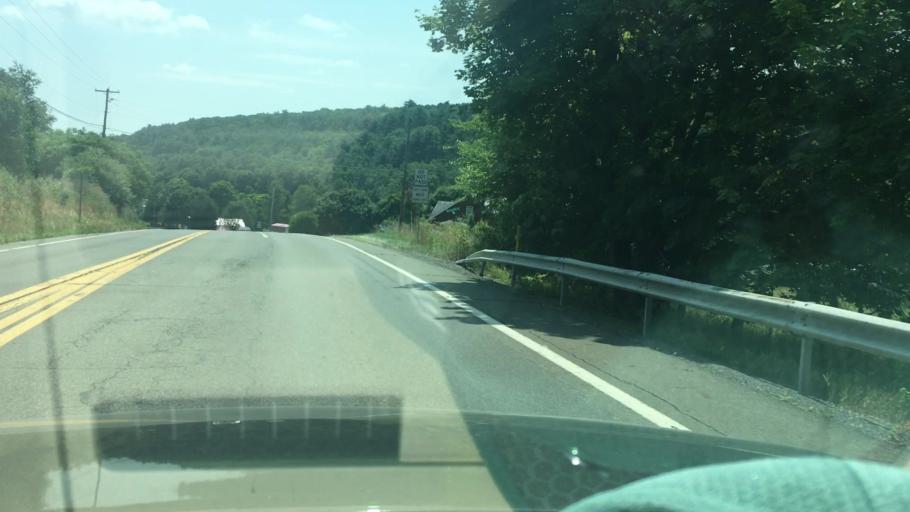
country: US
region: Pennsylvania
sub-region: Schuylkill County
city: Coaldale
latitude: 40.7430
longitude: -75.8930
